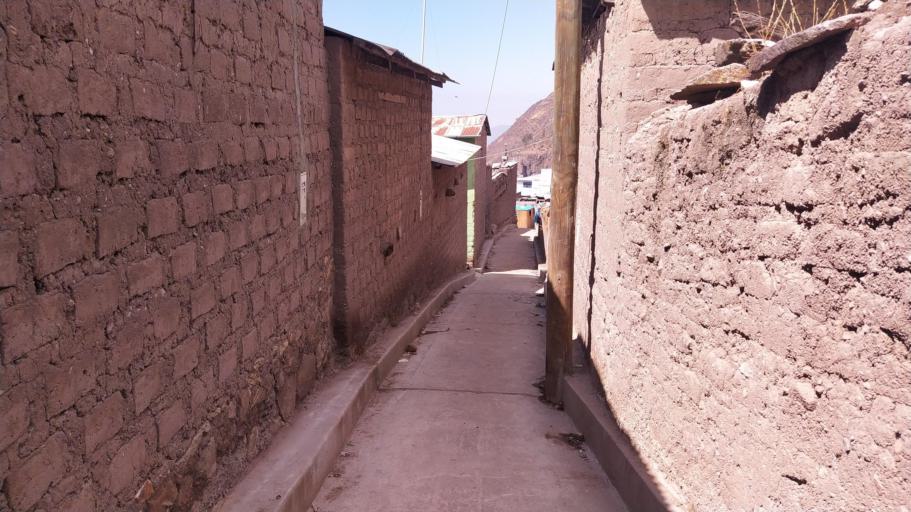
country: PE
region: Lima
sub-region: Provincia de Huarochiri
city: Cocachacra
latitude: -11.9997
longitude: -76.4742
